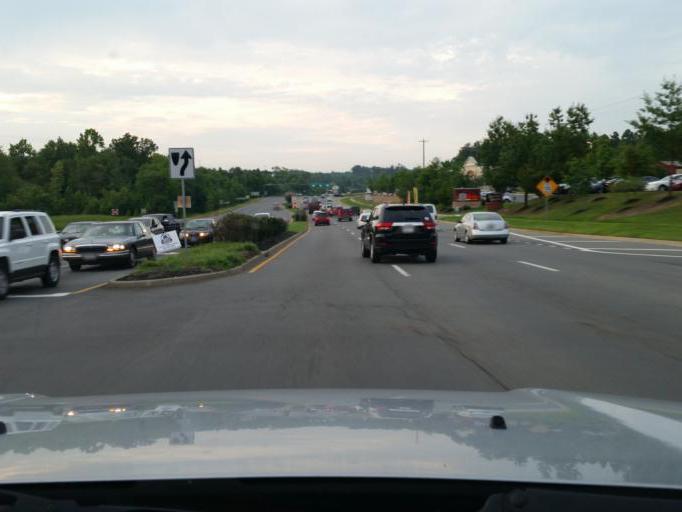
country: US
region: Virginia
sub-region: Spotsylvania County
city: Spotsylvania Courthouse
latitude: 38.2262
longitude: -77.5055
